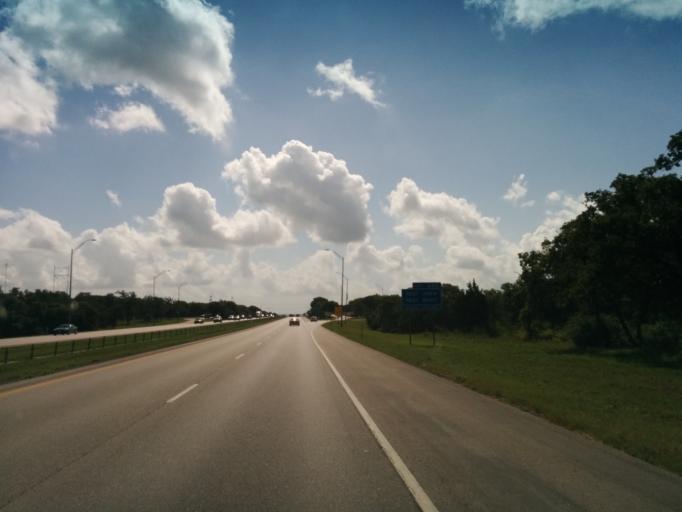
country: US
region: Texas
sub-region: Colorado County
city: Columbus
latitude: 29.6932
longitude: -96.6146
